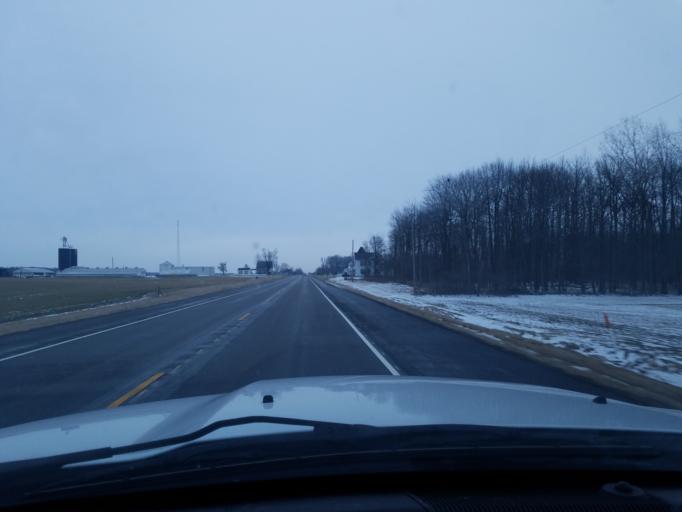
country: US
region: Indiana
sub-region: Randolph County
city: Parker City
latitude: 40.1932
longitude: -85.1905
